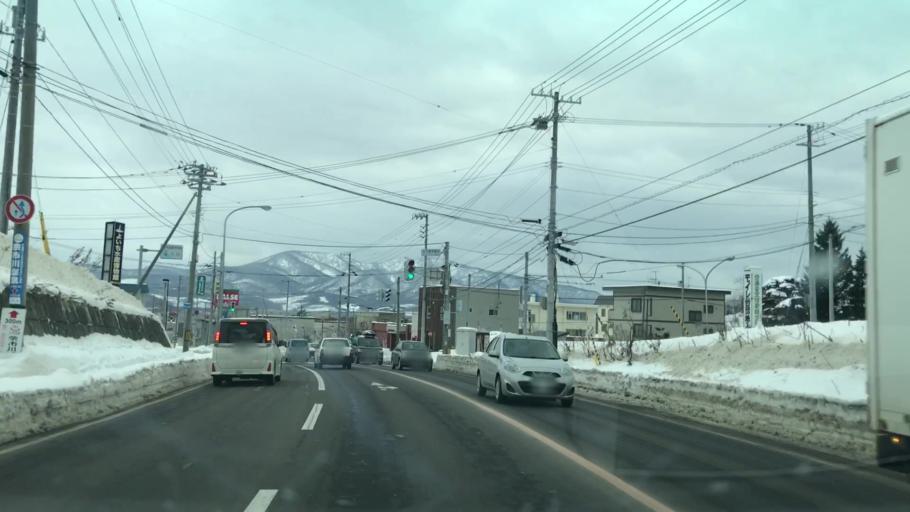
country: JP
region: Hokkaido
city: Yoichi
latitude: 43.1960
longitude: 140.7847
